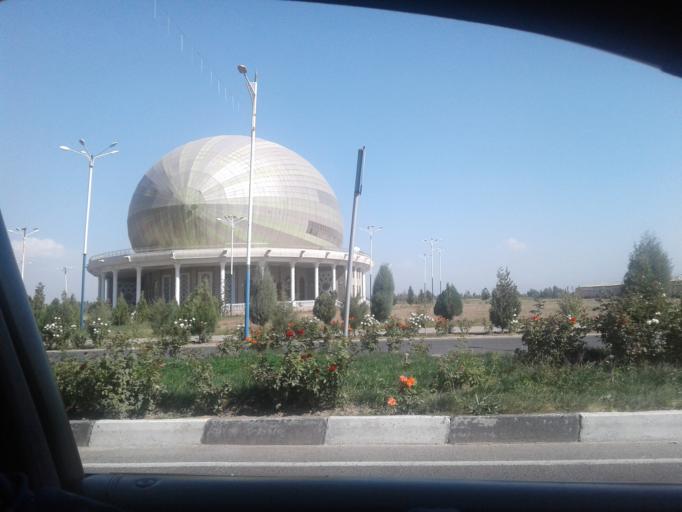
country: TJ
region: Republican Subordination
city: Hisor
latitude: 38.5389
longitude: 68.5586
